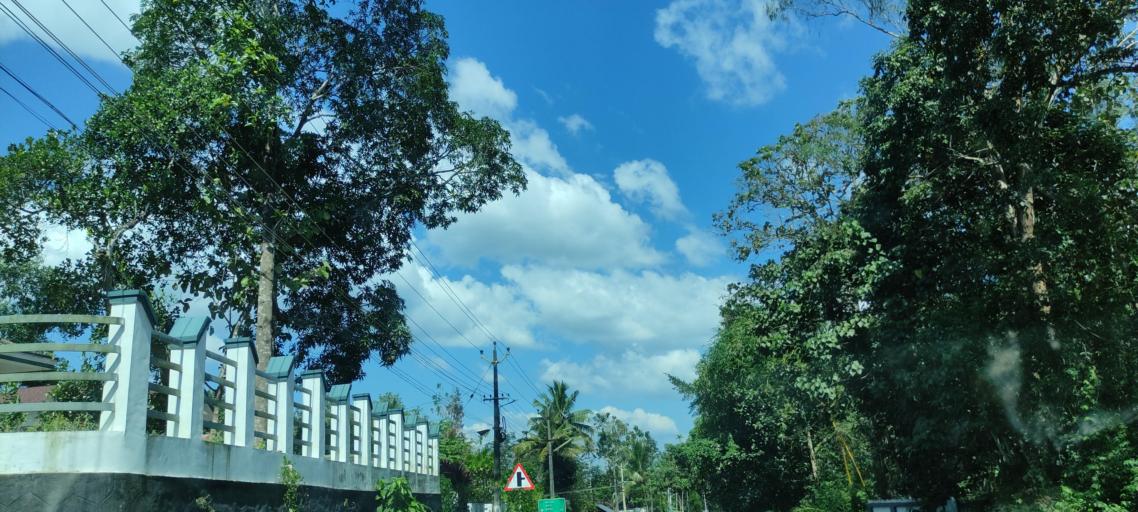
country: IN
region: Kerala
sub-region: Pattanamtitta
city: Adur
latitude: 9.1122
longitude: 76.6966
